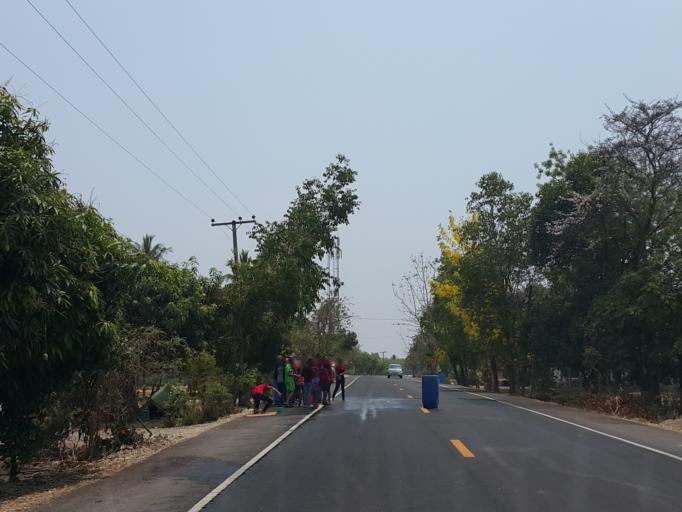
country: TH
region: Kamphaeng Phet
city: Pang Sila Thong
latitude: 16.0332
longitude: 99.3734
